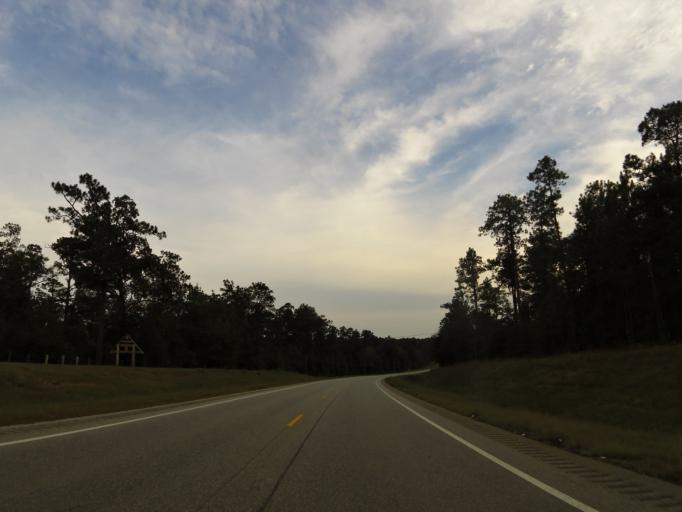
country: US
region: Alabama
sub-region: Monroe County
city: Frisco City
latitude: 31.2596
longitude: -87.4938
